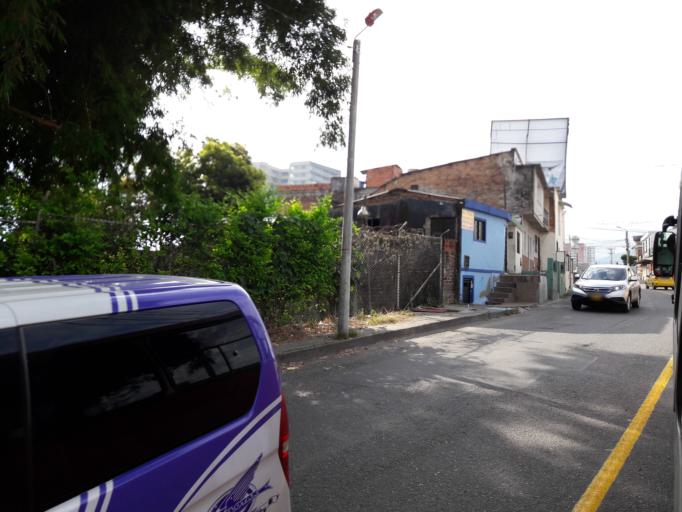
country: CO
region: Tolima
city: Ibague
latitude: 4.4358
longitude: -75.2107
